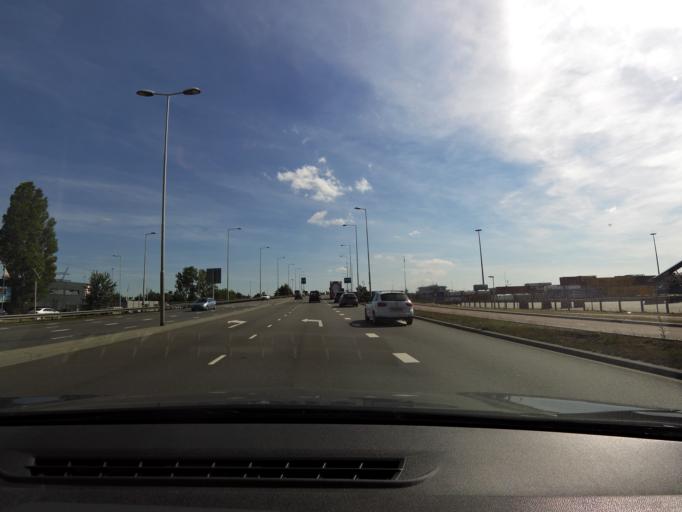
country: NL
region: South Holland
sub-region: Gemeente Albrandswaard
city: Rhoon
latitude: 51.8744
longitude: 4.4305
